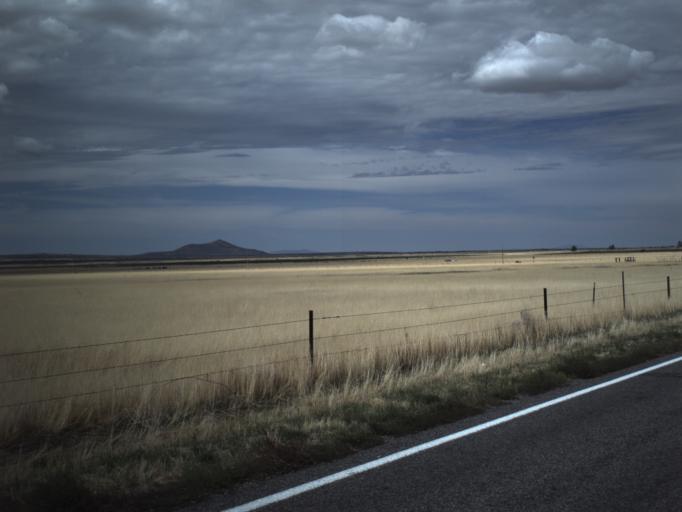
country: US
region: Utah
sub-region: Millard County
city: Fillmore
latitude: 39.0203
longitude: -112.4100
